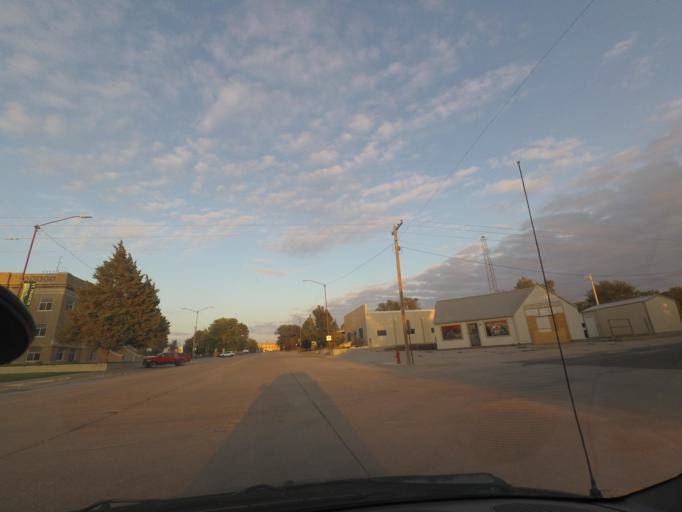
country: US
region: Kansas
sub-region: Cheyenne County
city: Saint Francis
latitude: 39.7742
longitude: -101.8004
